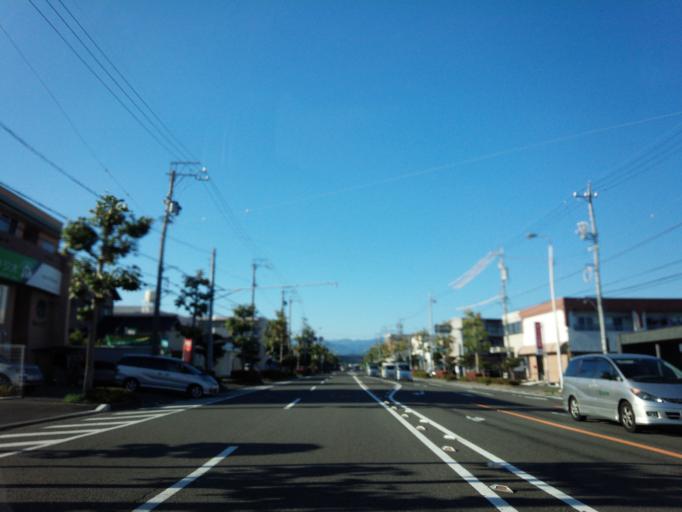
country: JP
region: Shizuoka
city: Shizuoka-shi
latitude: 34.9555
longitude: 138.4192
